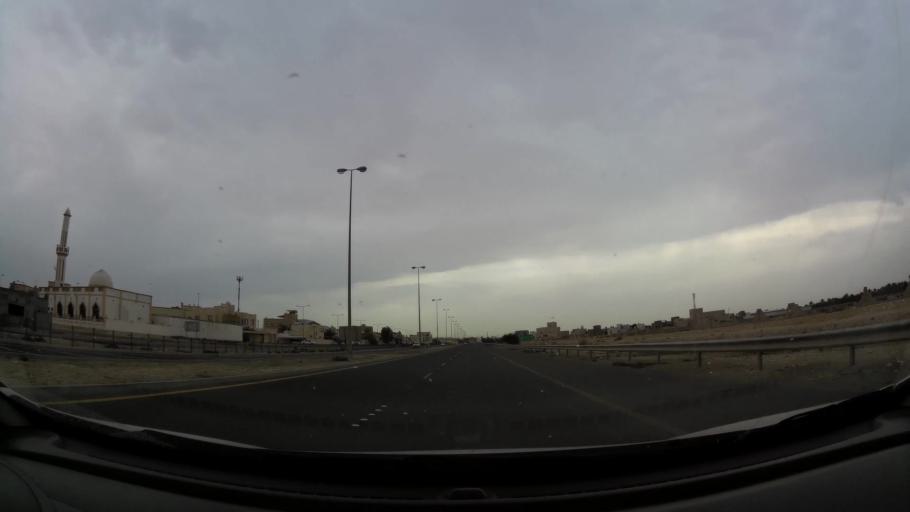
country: BH
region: Central Governorate
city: Madinat Hamad
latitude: 26.1125
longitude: 50.4937
